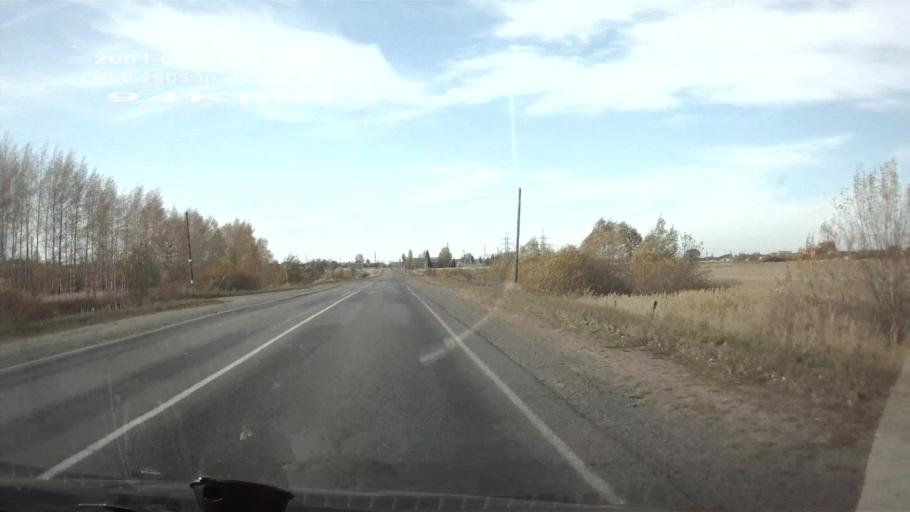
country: RU
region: Chuvashia
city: Ibresi
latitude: 55.2902
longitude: 47.0620
